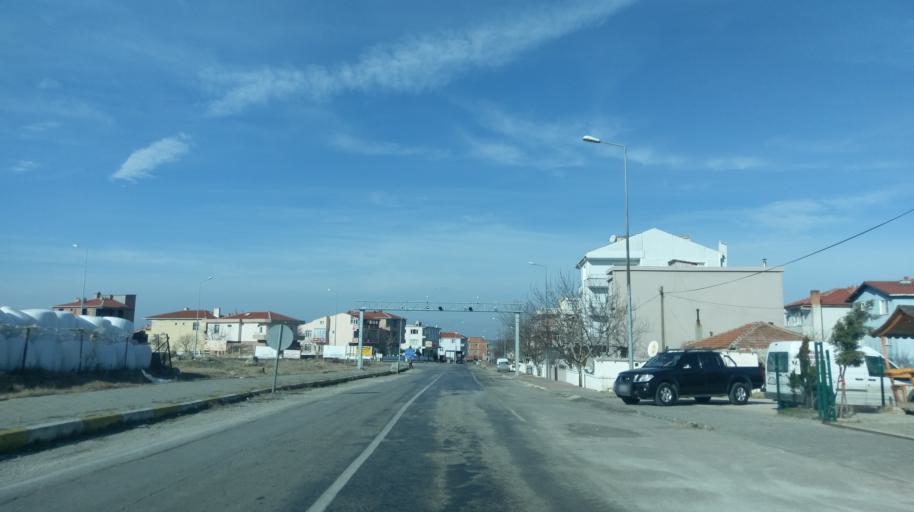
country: TR
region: Edirne
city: Uzun Keupru
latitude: 41.2682
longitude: 26.7071
